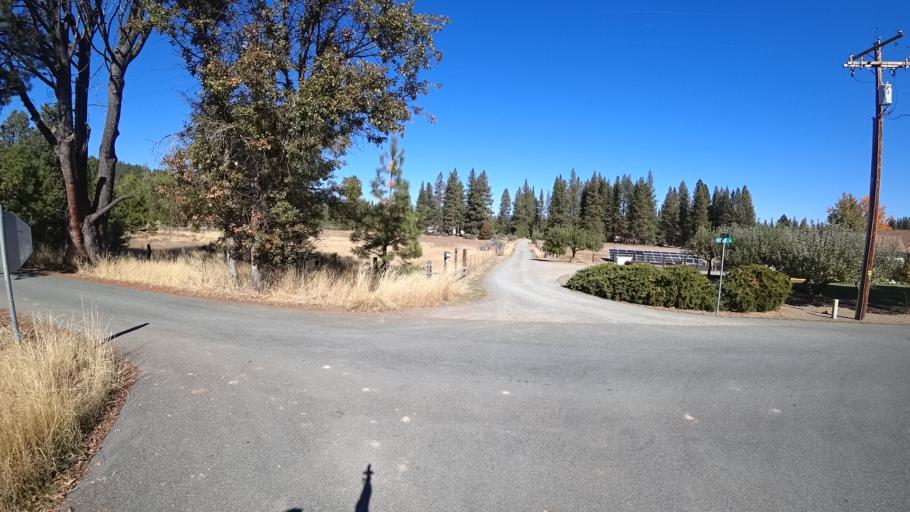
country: US
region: California
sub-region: Siskiyou County
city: Yreka
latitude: 41.5266
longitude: -122.9192
